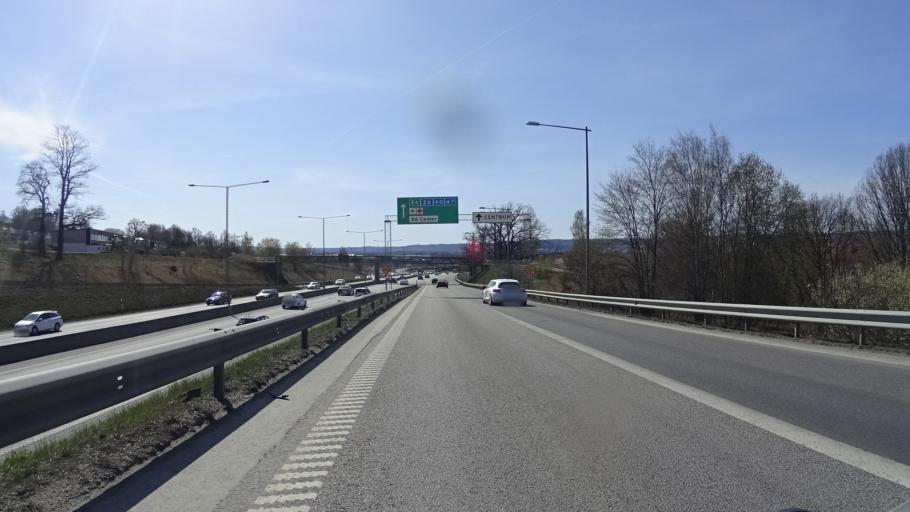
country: SE
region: Joenkoeping
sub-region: Jonkopings Kommun
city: Jonkoping
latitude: 57.7782
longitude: 14.2193
